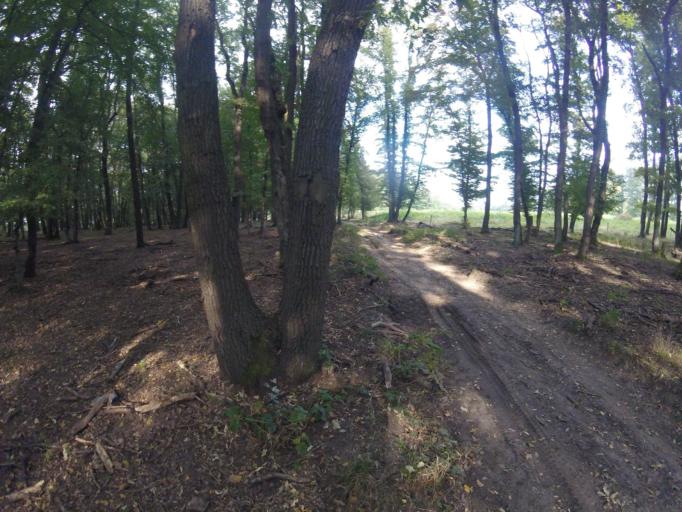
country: HU
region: Komarom-Esztergom
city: Pilismarot
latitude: 47.7908
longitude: 18.8208
